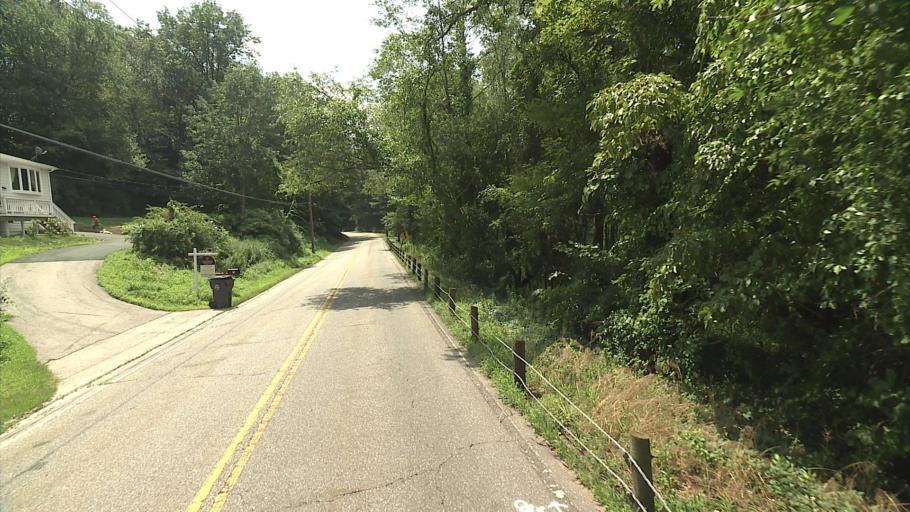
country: US
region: Connecticut
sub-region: New London County
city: Baltic
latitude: 41.5997
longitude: -72.1272
